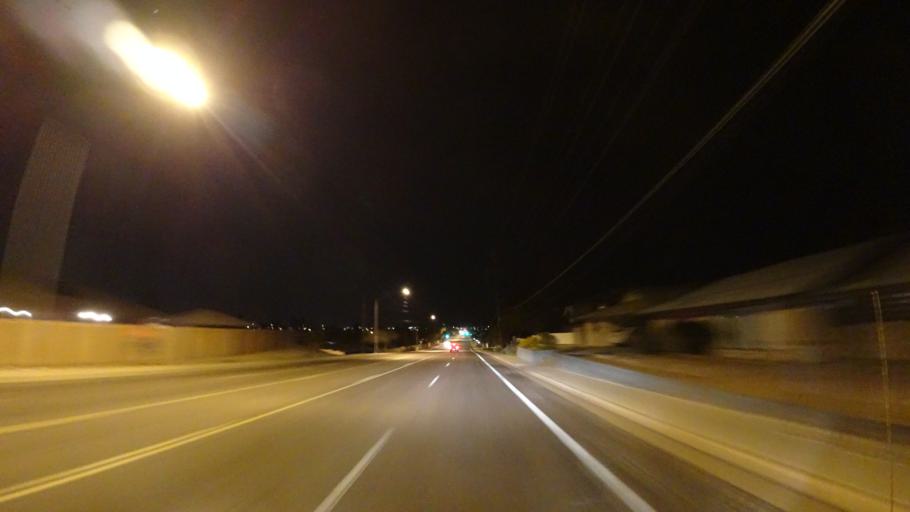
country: US
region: Arizona
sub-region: Maricopa County
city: Mesa
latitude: 33.4410
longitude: -111.8312
